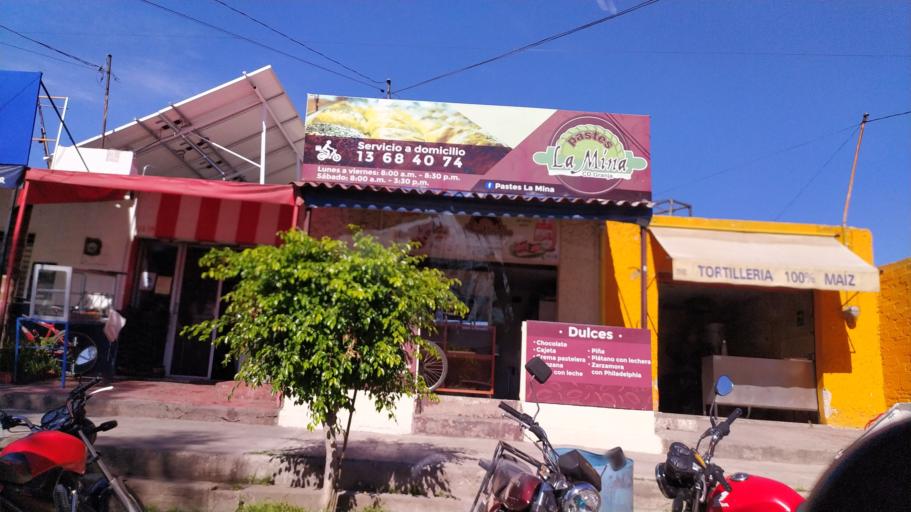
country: MX
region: Jalisco
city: Zapopan2
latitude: 20.6829
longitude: -103.4528
